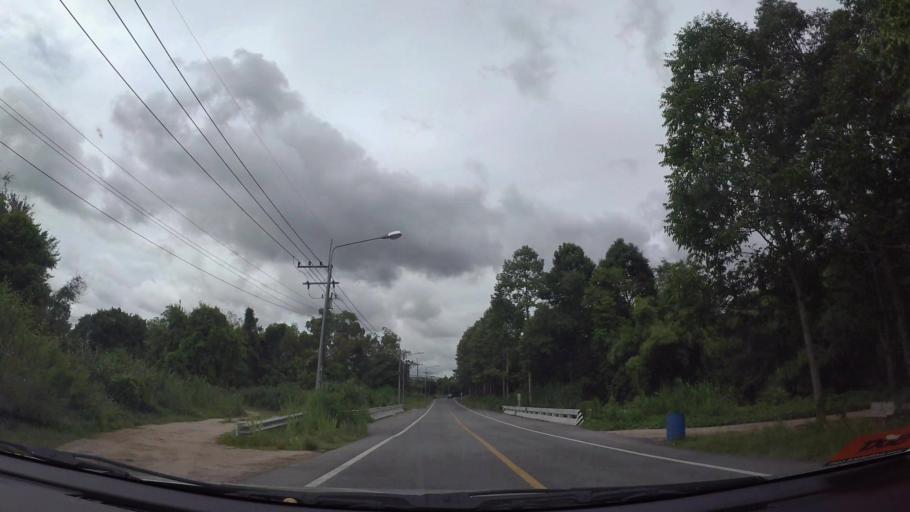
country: TH
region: Chon Buri
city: Si Racha
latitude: 13.1939
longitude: 100.9955
